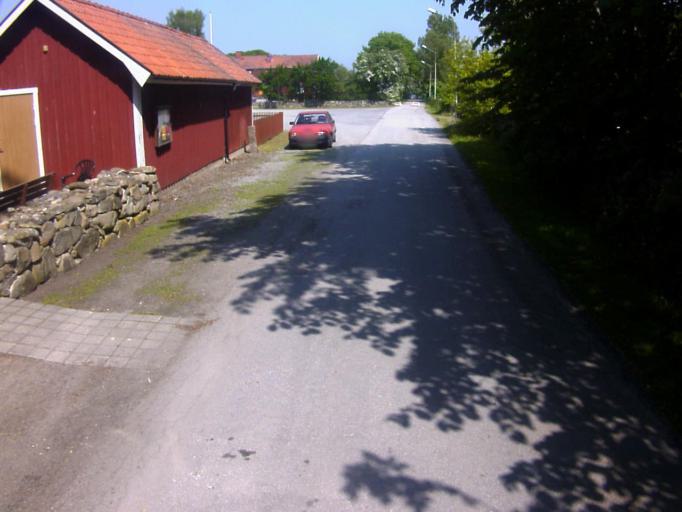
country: SE
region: Blekinge
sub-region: Karlshamns Kommun
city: Morrum
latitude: 56.1169
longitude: 14.6730
